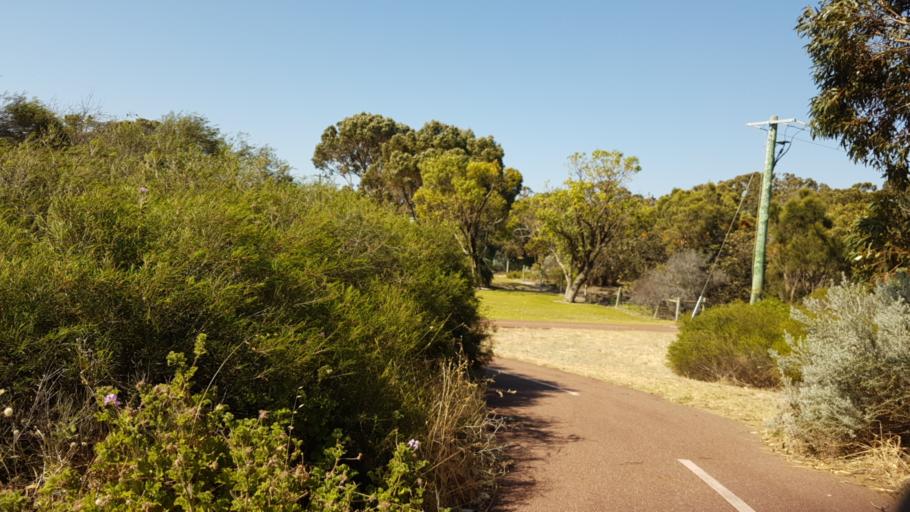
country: AU
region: Western Australia
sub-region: Stirling
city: North Beach
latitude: -31.8580
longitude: 115.7694
